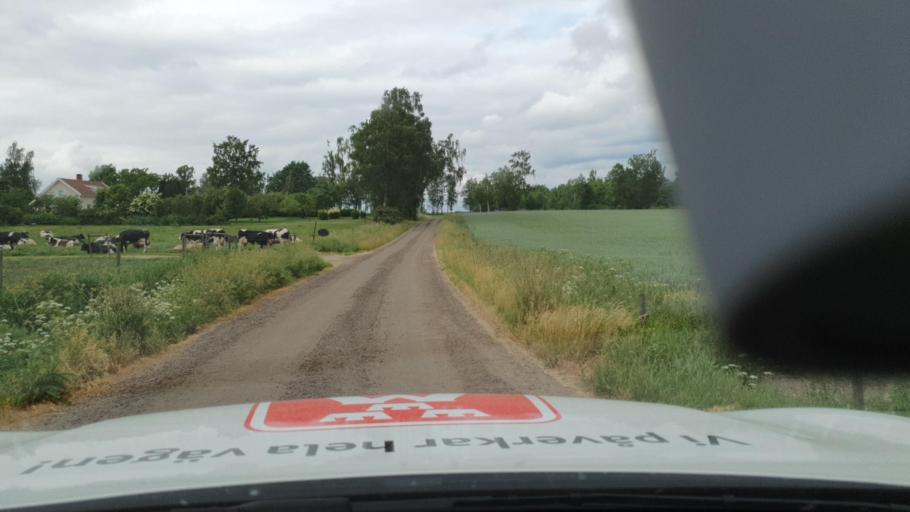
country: SE
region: Vaestra Goetaland
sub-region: Hjo Kommun
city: Hjo
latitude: 58.1975
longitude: 14.1760
